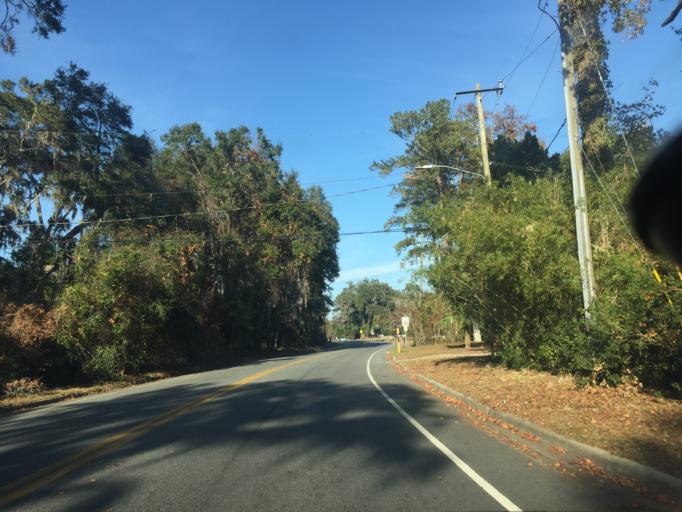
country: US
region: Georgia
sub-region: Chatham County
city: Montgomery
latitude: 31.9904
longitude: -81.1182
